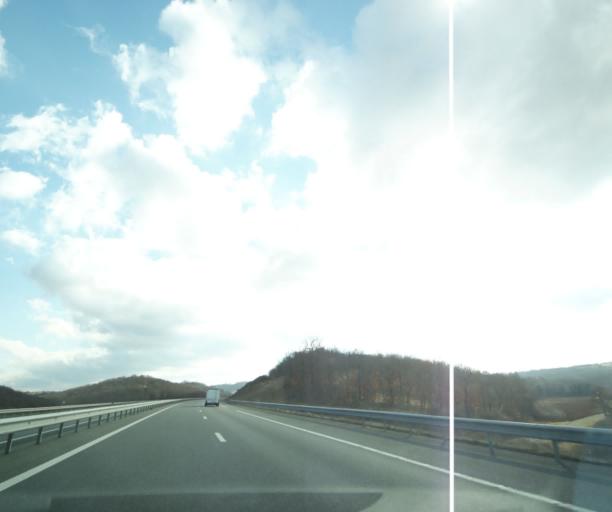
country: FR
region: Midi-Pyrenees
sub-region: Departement du Lot
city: Le Vigan
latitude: 44.7698
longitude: 1.5390
